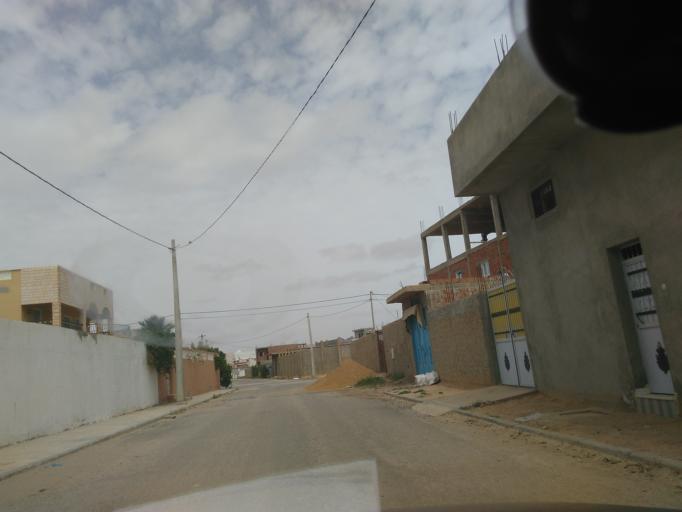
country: TN
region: Tataouine
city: Tataouine
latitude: 32.9482
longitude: 10.4687
